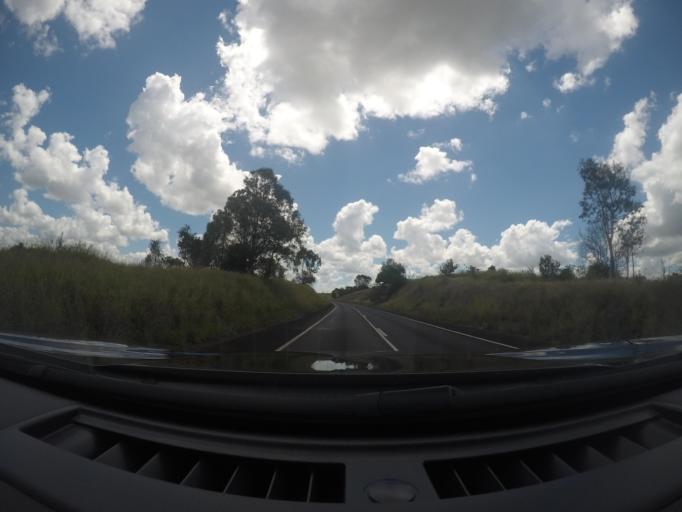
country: AU
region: Queensland
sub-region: Moreton Bay
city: Woodford
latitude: -27.1385
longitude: 152.5083
